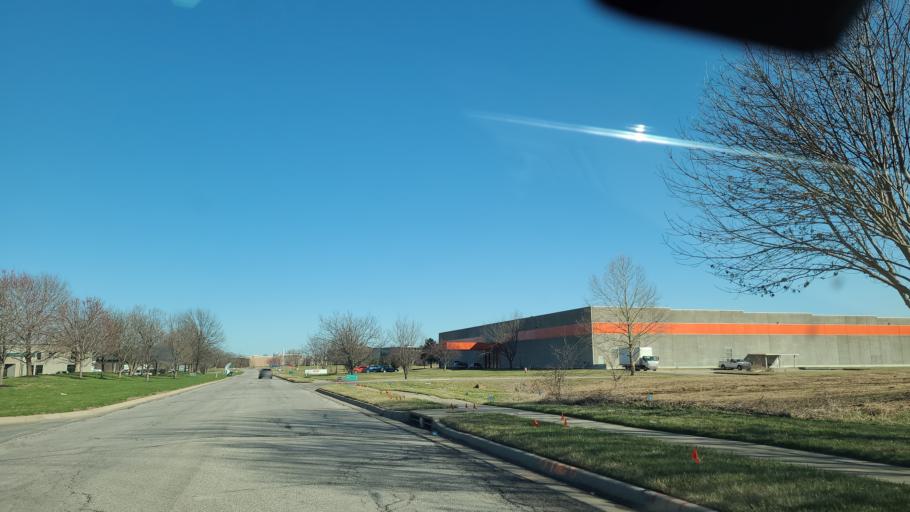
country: US
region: Kansas
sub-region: Douglas County
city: Lawrence
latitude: 38.9482
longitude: -95.1865
